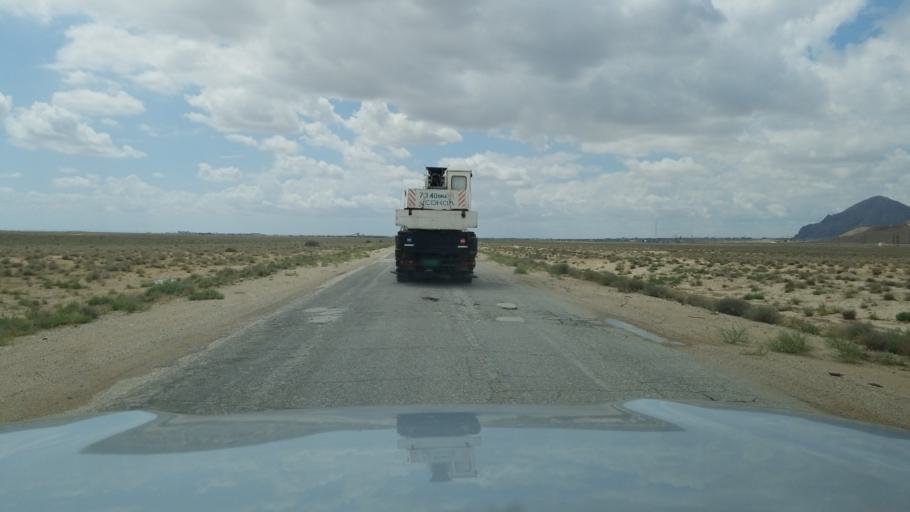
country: TM
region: Balkan
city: Balkanabat
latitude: 39.4835
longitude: 54.4351
